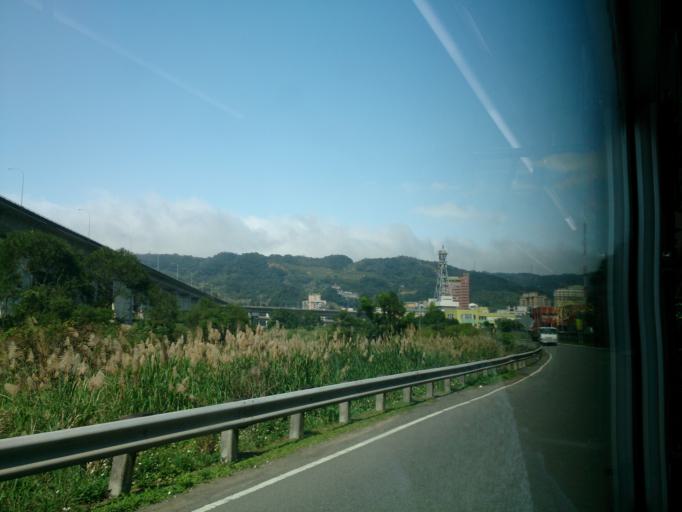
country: TW
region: Taipei
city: Taipei
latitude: 24.9975
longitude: 121.5948
